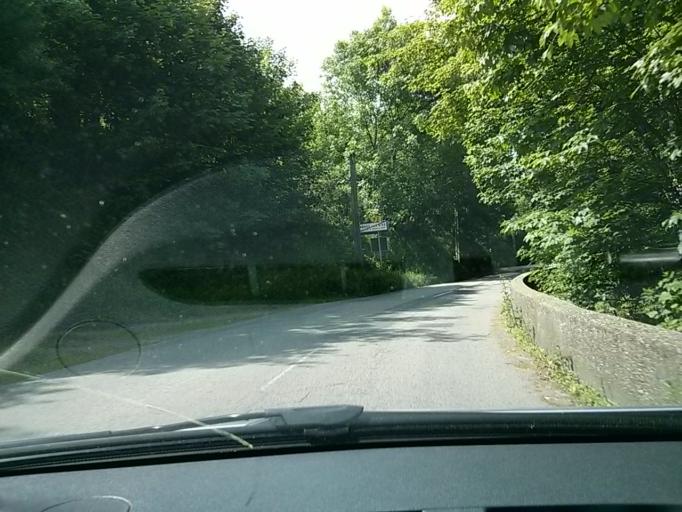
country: FR
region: Rhone-Alpes
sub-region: Departement de la Loire
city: Saint-Chamond
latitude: 45.4275
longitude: 4.5141
